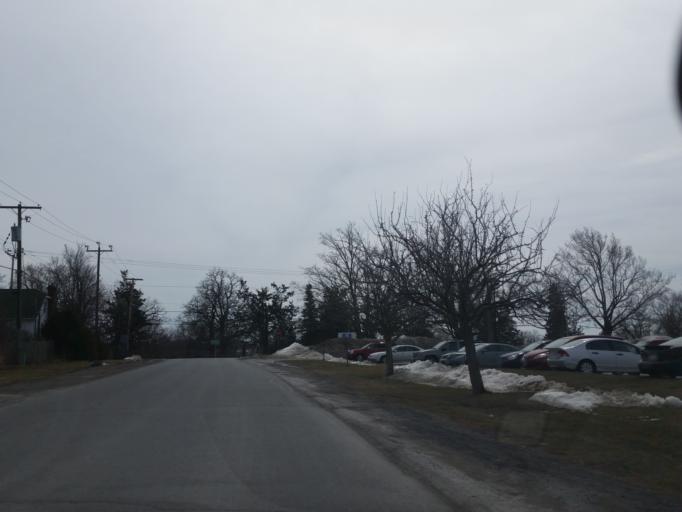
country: CA
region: Ontario
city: Napanee Downtown
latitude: 44.2401
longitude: -76.9657
